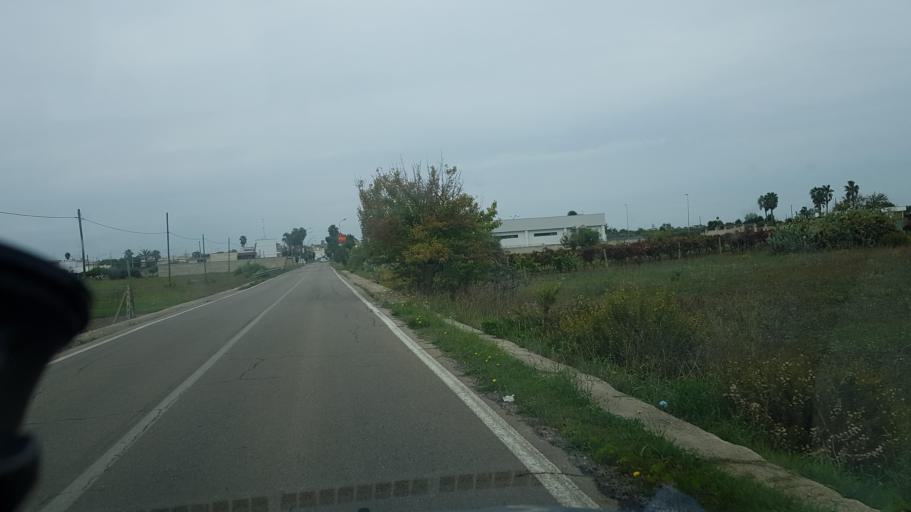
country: IT
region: Apulia
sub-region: Provincia di Lecce
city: Veglie
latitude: 40.3265
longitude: 17.9756
